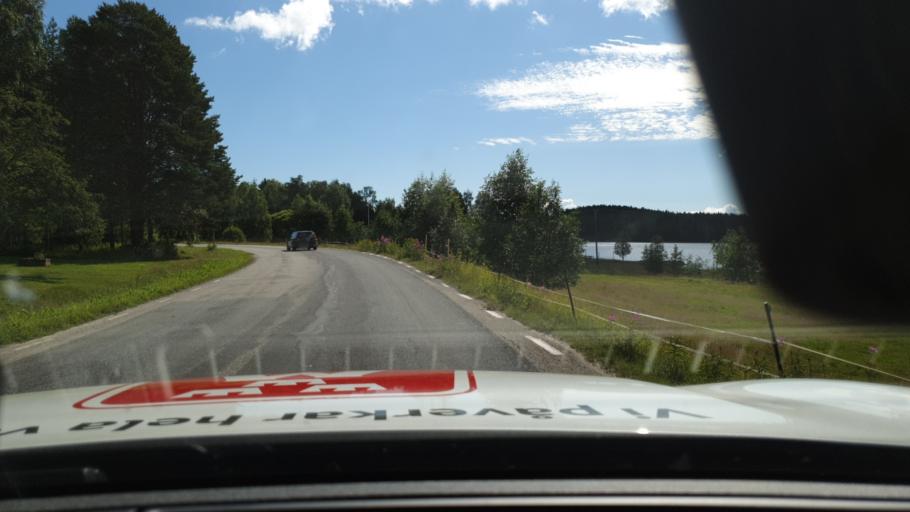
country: SE
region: Norrbotten
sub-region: Lulea Kommun
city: Ranea
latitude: 65.7734
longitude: 22.2468
